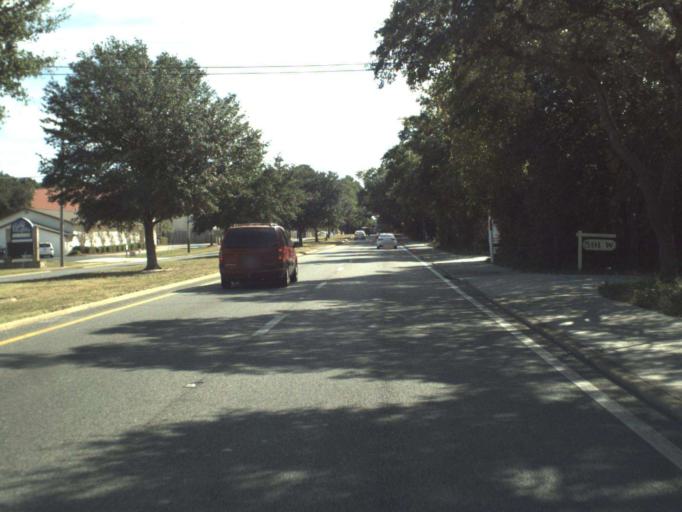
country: US
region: Florida
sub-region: Okaloosa County
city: Mary Esther
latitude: 30.4101
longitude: -86.6778
